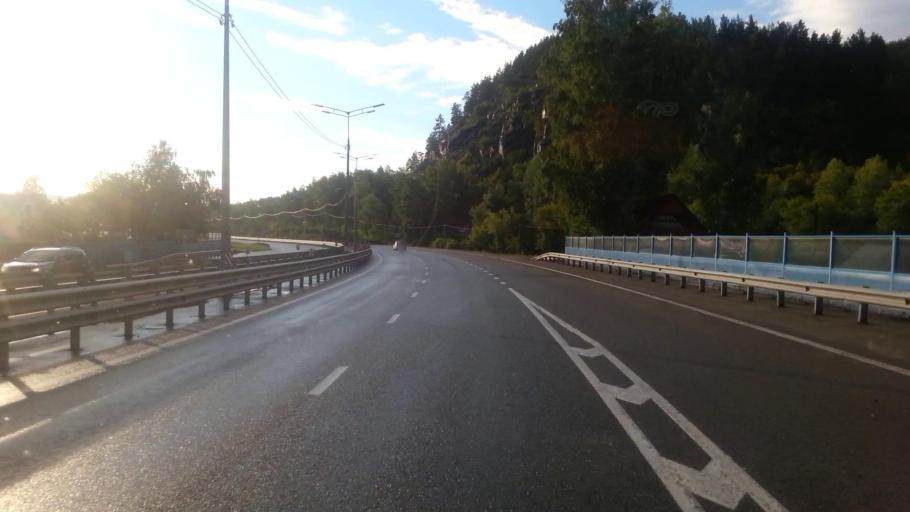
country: RU
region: Altay
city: Souzga
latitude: 51.9184
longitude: 85.8588
